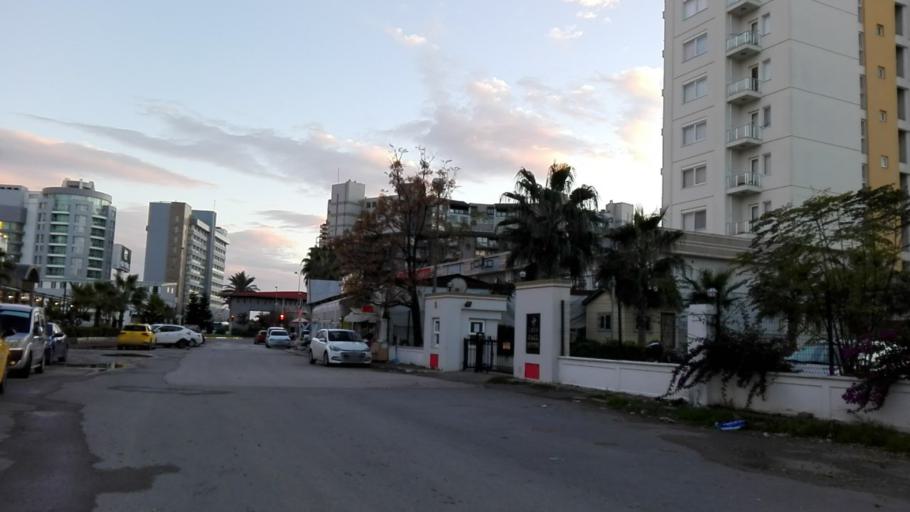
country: TR
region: Antalya
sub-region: Serik
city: Kumkoey
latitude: 36.8581
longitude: 30.8808
